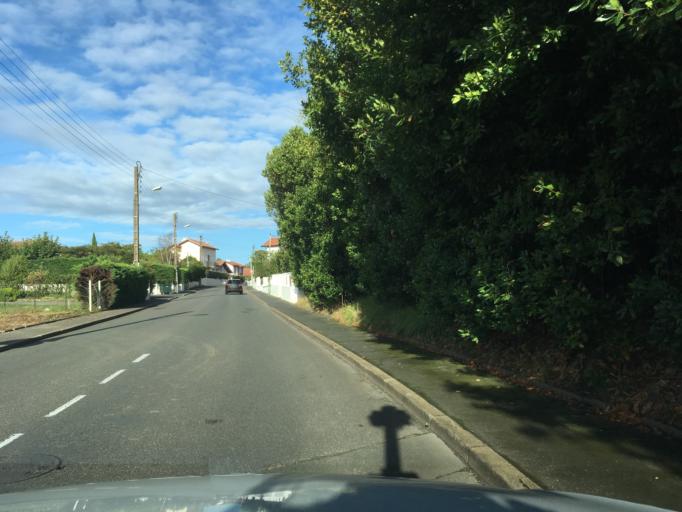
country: FR
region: Aquitaine
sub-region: Departement des Pyrenees-Atlantiques
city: Biarritz
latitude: 43.4629
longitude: -1.5587
